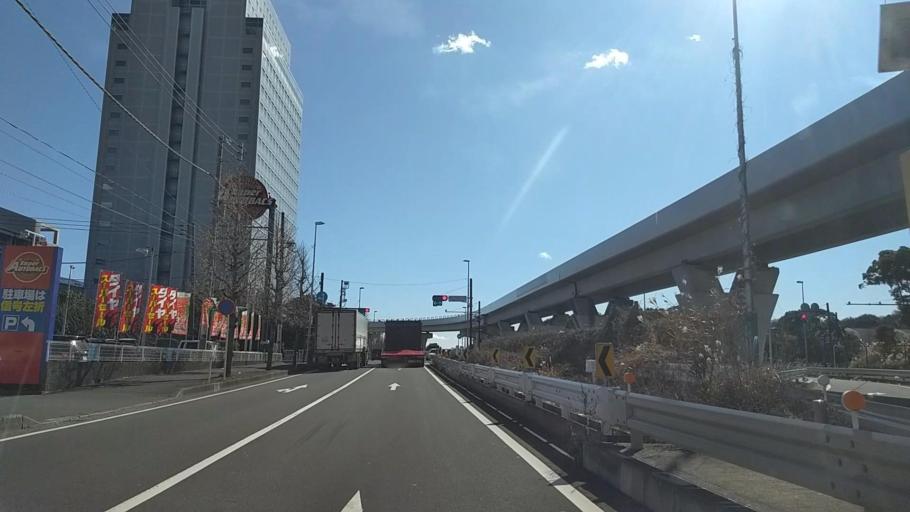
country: JP
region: Kanagawa
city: Yokosuka
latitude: 35.3556
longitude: 139.6441
